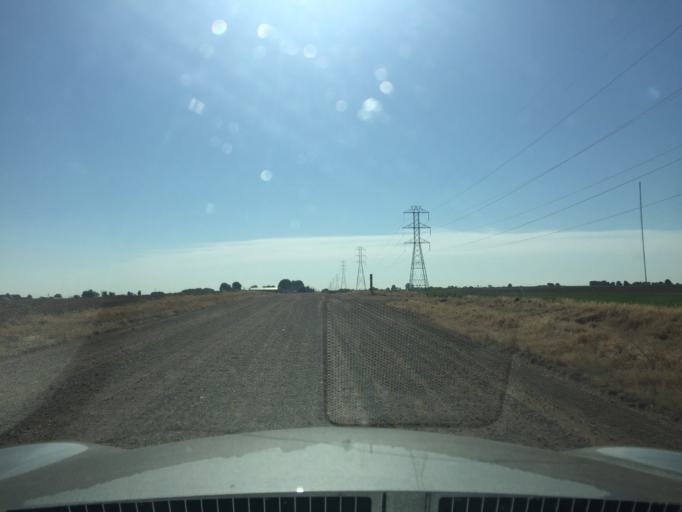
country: US
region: Colorado
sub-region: Boulder County
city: Erie
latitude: 40.0584
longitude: -105.0234
